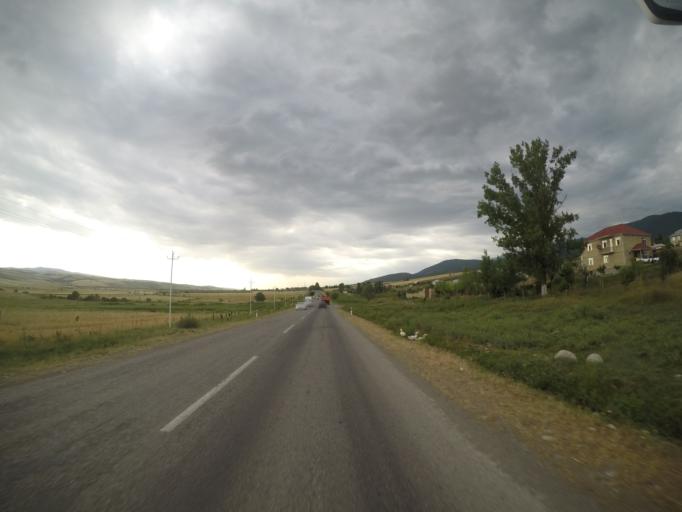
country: AZ
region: Ismayilli
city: Ismayilli
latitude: 40.7390
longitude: 48.2613
